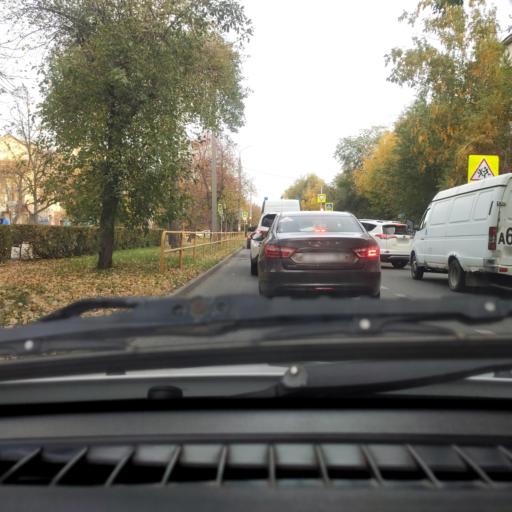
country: RU
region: Samara
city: Tol'yatti
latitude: 53.5048
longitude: 49.4133
